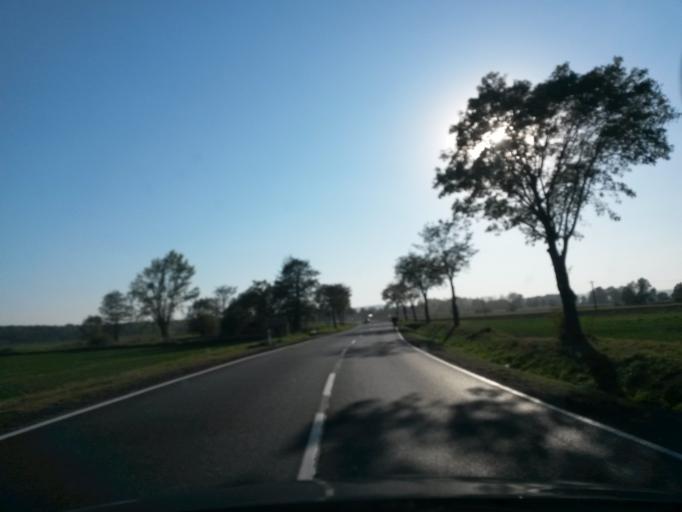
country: PL
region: Lower Silesian Voivodeship
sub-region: Powiat swidnicki
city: Strzegom
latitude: 50.9391
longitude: 16.3206
